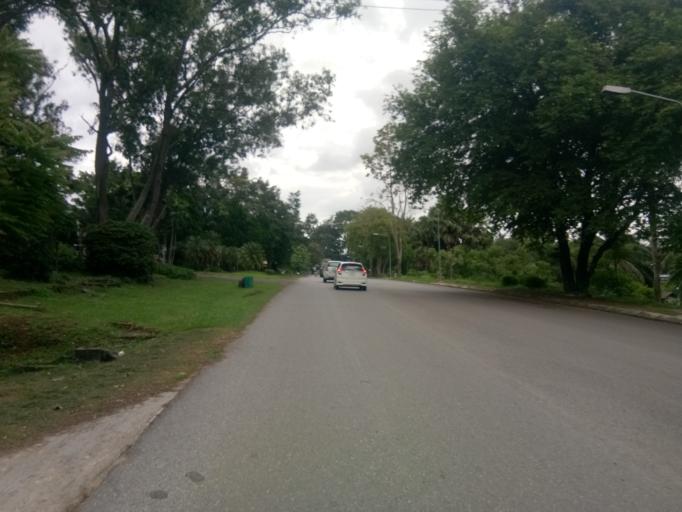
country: TH
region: Chiang Rai
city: Chiang Rai
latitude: 19.9830
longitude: 99.8495
